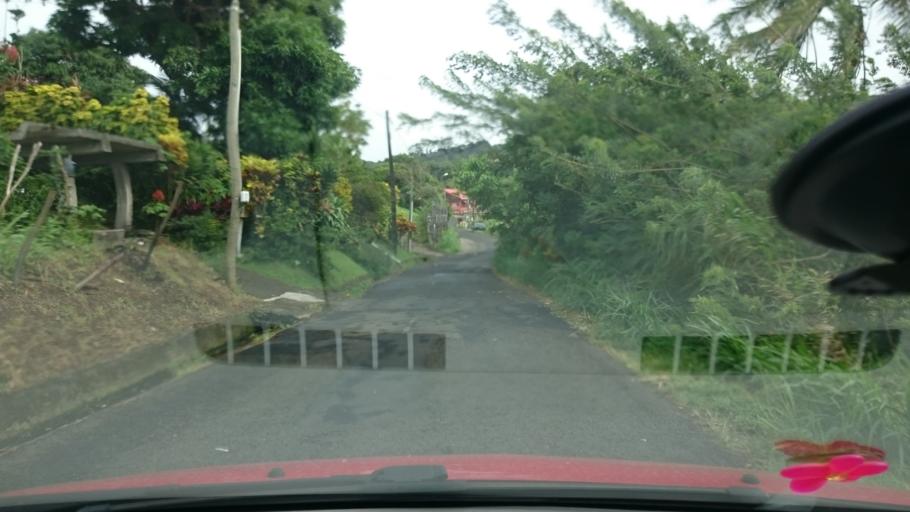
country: MQ
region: Martinique
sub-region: Martinique
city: Sainte-Luce
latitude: 14.4899
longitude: -60.9242
